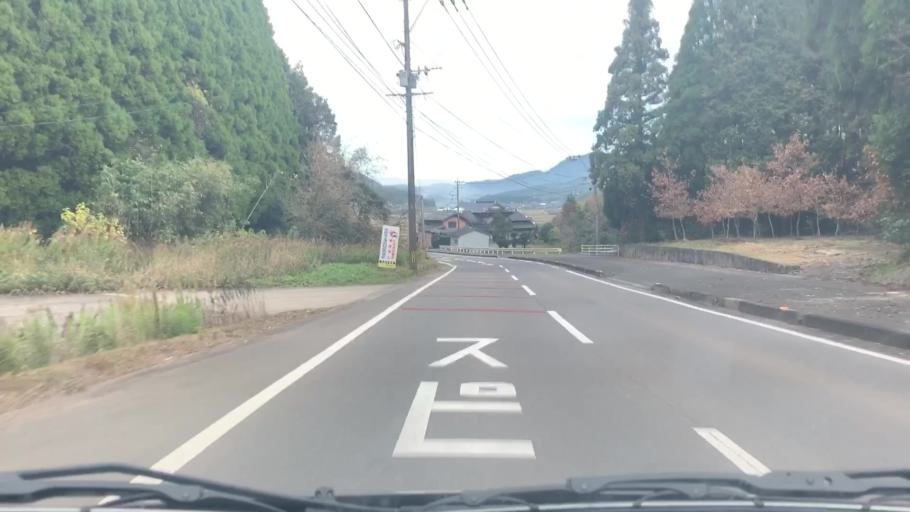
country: JP
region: Saga Prefecture
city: Takeocho-takeo
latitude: 33.2110
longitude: 129.9631
